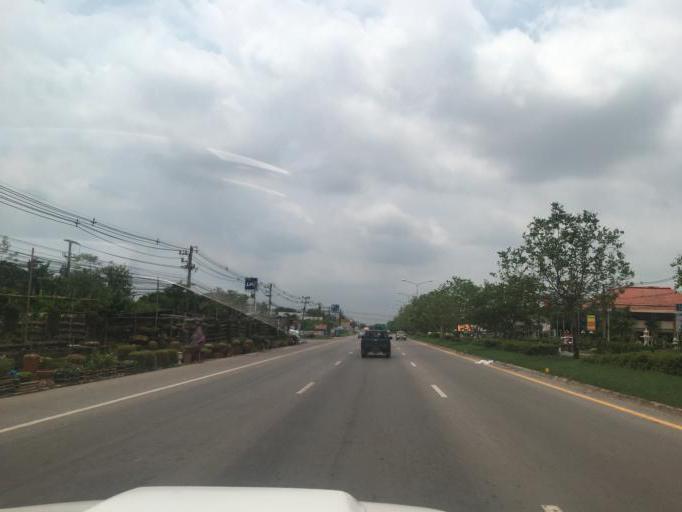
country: TH
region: Changwat Udon Thani
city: Udon Thani
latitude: 17.3962
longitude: 102.7661
